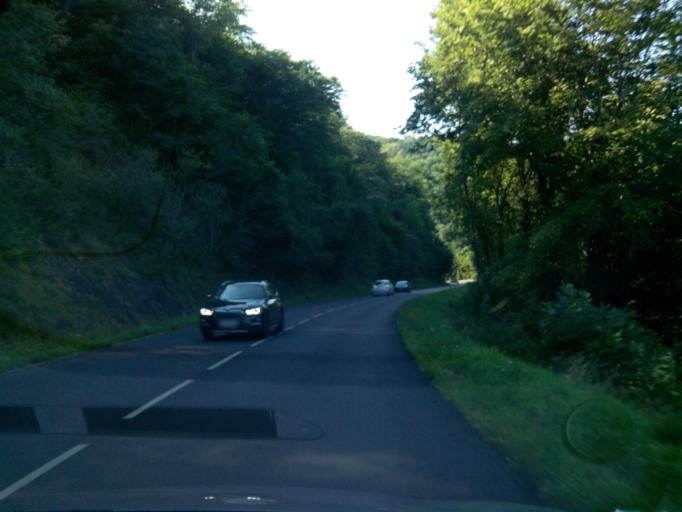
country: FR
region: Limousin
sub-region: Departement de la Correze
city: Beynat
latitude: 45.1312
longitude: 1.6777
